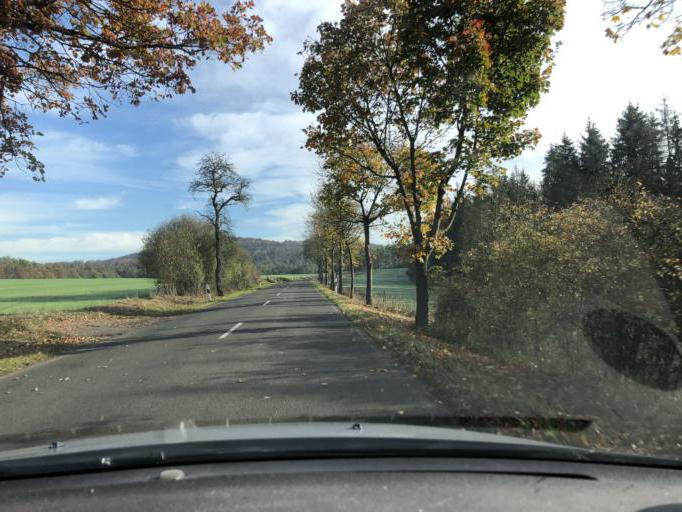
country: DE
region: Thuringia
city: Reurieth
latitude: 50.4358
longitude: 10.6373
